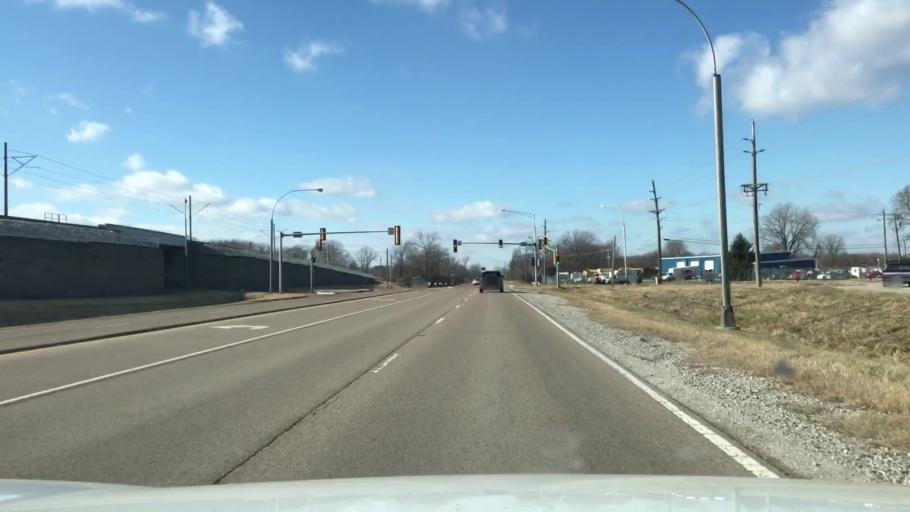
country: US
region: Illinois
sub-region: Saint Clair County
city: Washington Park
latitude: 38.6036
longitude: -90.0634
